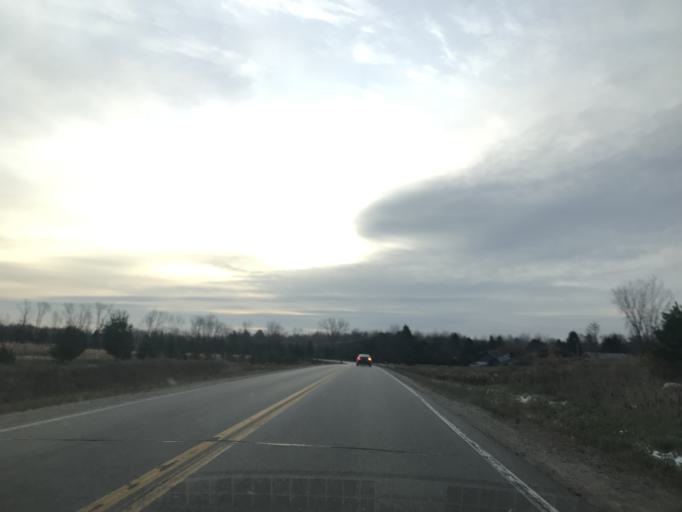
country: US
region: Wisconsin
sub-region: Marinette County
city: Peshtigo
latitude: 45.0599
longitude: -87.7963
